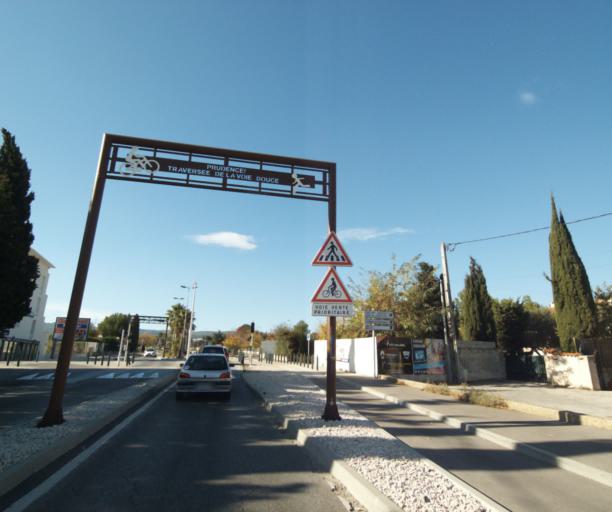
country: FR
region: Provence-Alpes-Cote d'Azur
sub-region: Departement des Bouches-du-Rhone
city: La Ciotat
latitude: 43.1923
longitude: 5.6155
